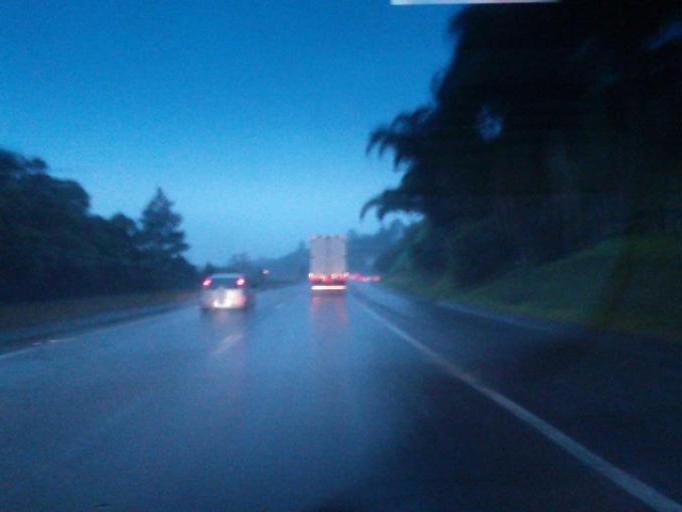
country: BR
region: Sao Paulo
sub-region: Juquitiba
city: Juquitiba
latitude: -23.9403
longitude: -47.0464
